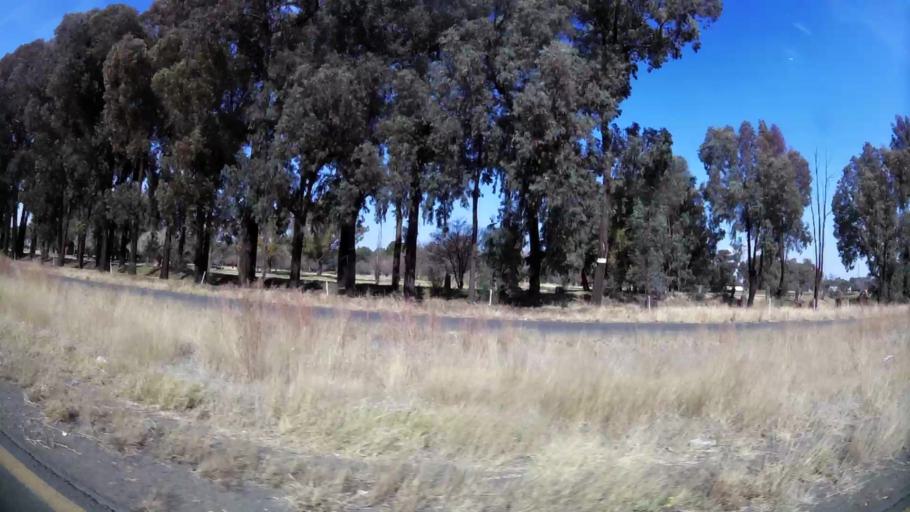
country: ZA
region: Orange Free State
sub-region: Mangaung Metropolitan Municipality
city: Bloemfontein
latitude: -29.1162
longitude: 26.2462
